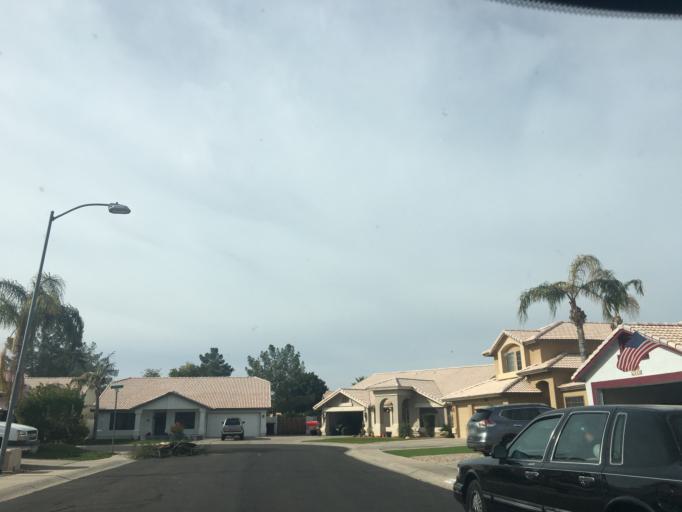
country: US
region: Arizona
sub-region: Maricopa County
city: Gilbert
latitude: 33.3458
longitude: -111.8021
